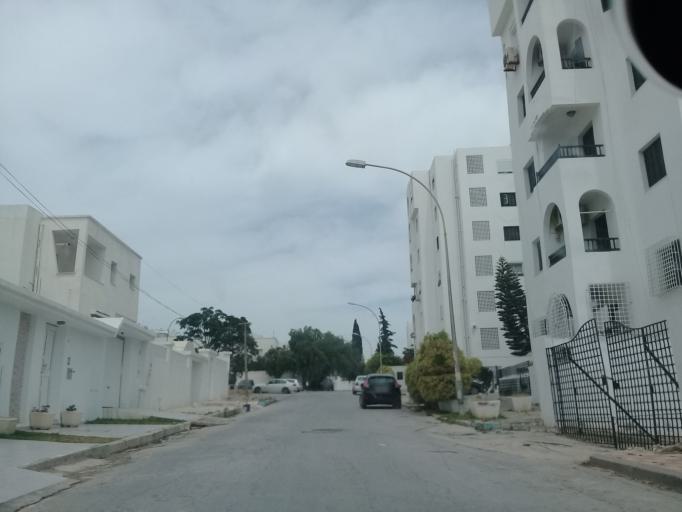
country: TN
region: Tunis
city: Tunis
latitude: 36.8357
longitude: 10.1566
